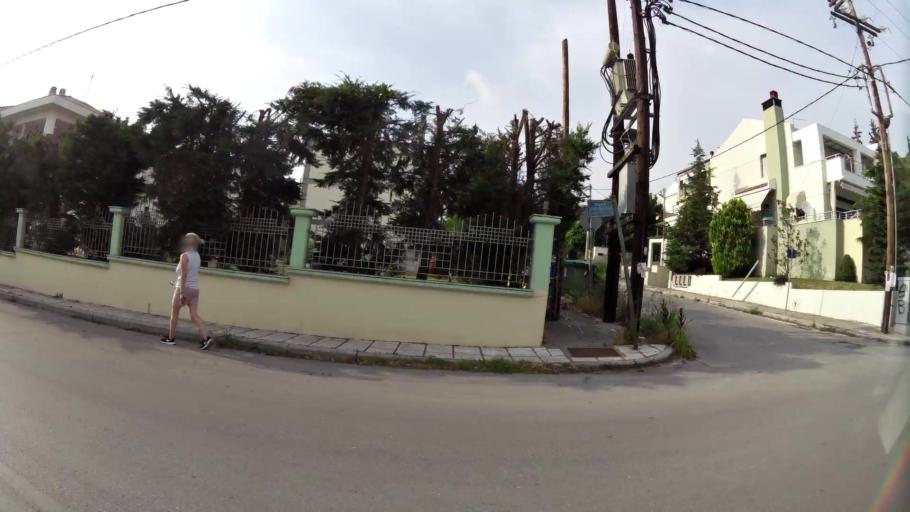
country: GR
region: Central Macedonia
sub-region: Nomos Thessalonikis
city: Oraiokastro
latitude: 40.7254
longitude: 22.9216
